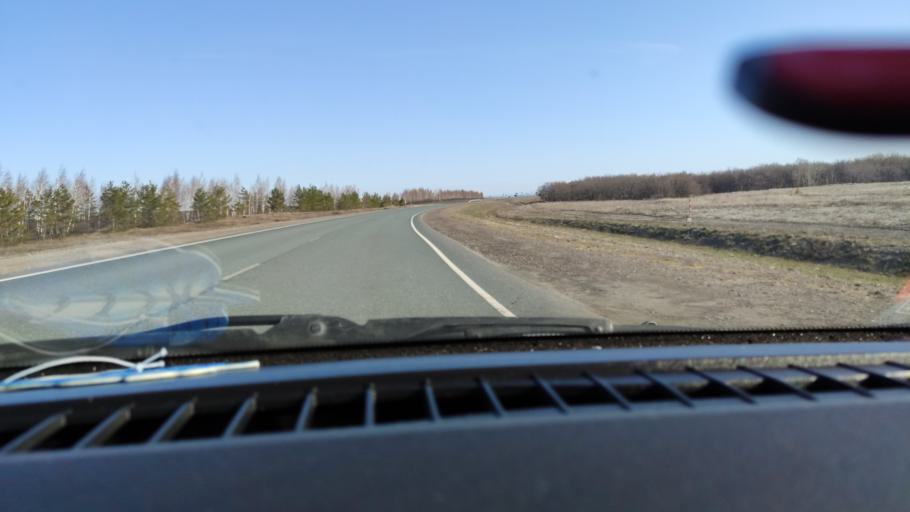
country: RU
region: Samara
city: Syzran'
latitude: 52.9456
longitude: 48.3047
